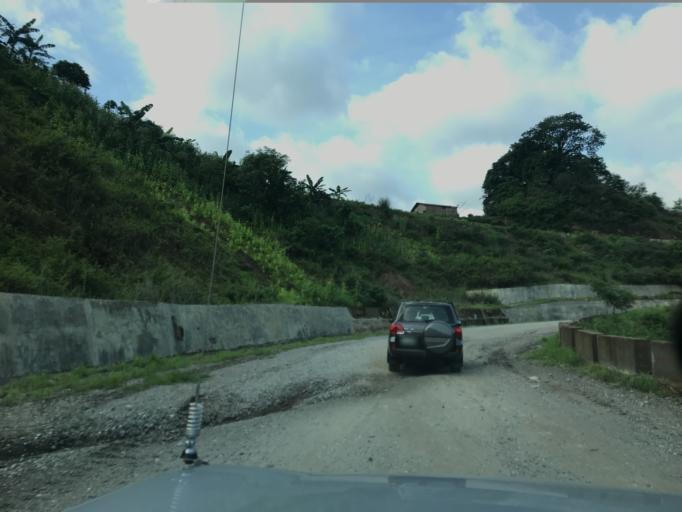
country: TL
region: Dili
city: Dili
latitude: -8.6375
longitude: 125.5084
